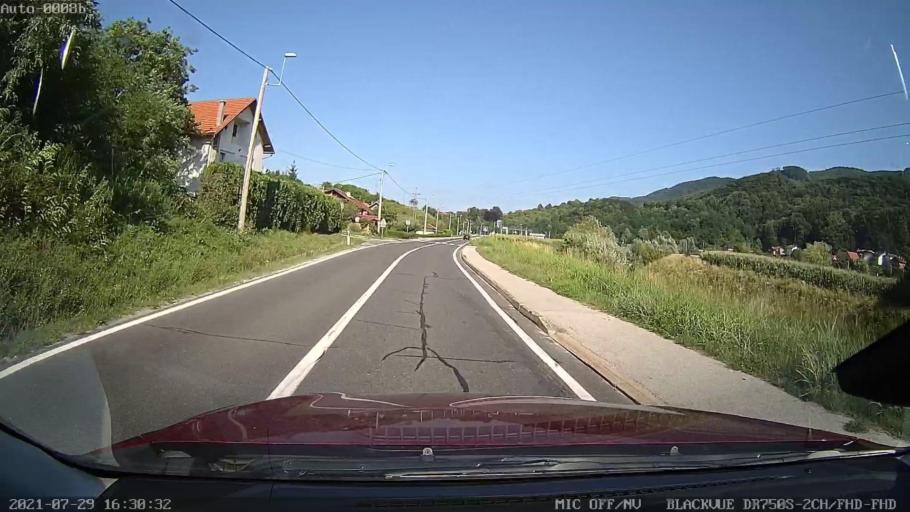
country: HR
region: Varazdinska
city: Lepoglava
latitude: 46.2090
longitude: 16.0250
